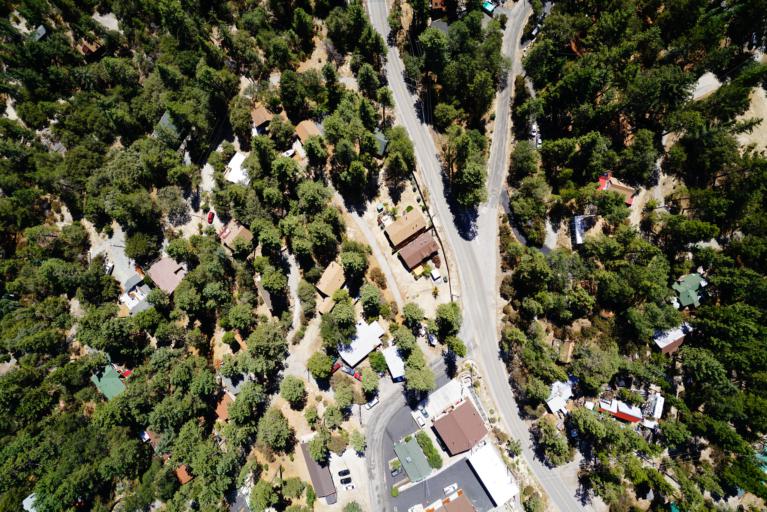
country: US
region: California
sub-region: Riverside County
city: Idyllwild-Pine Cove
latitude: 33.7605
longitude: -116.7375
